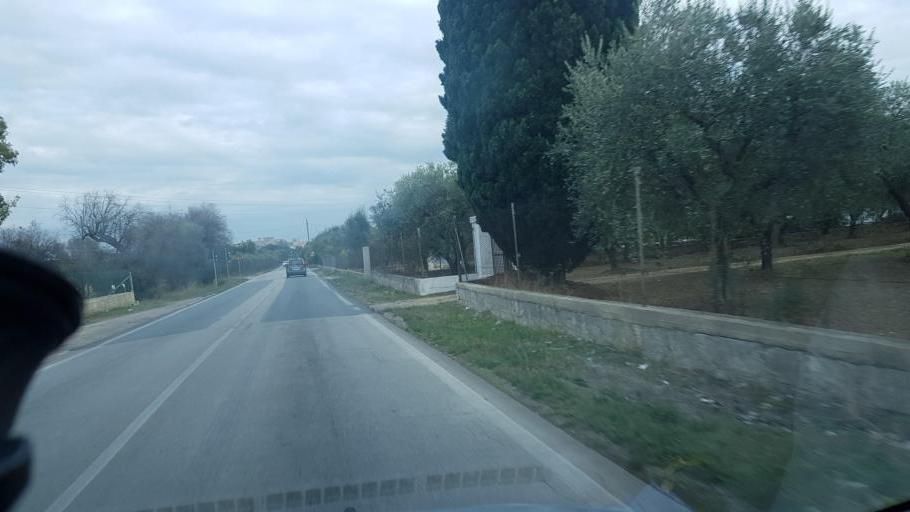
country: IT
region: Apulia
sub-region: Provincia di Brindisi
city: Oria
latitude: 40.5098
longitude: 17.6241
